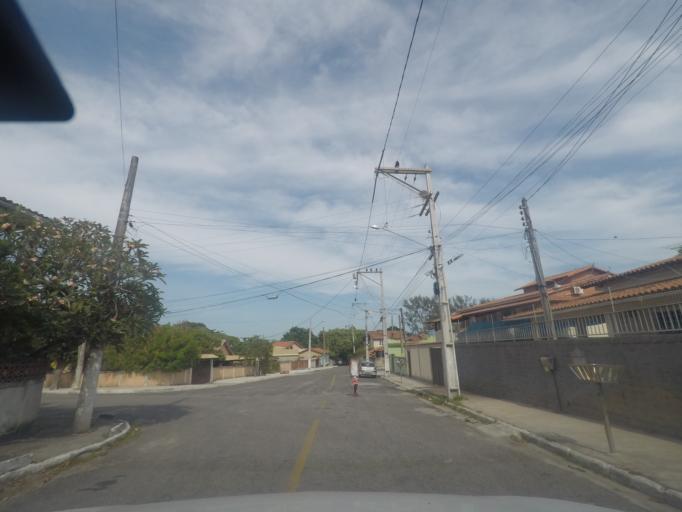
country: BR
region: Rio de Janeiro
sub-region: Marica
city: Marica
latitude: -22.9545
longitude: -42.8108
